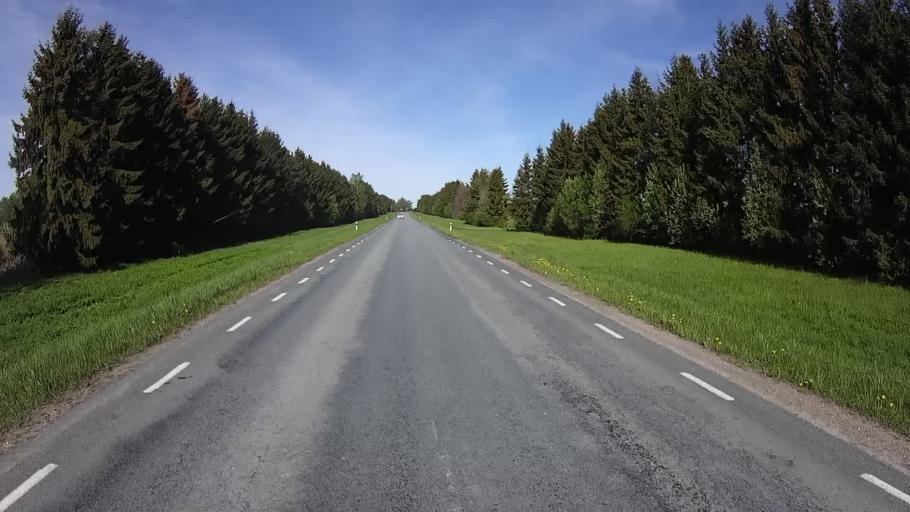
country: EE
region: Polvamaa
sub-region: Polva linn
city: Polva
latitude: 58.2233
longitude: 27.0459
